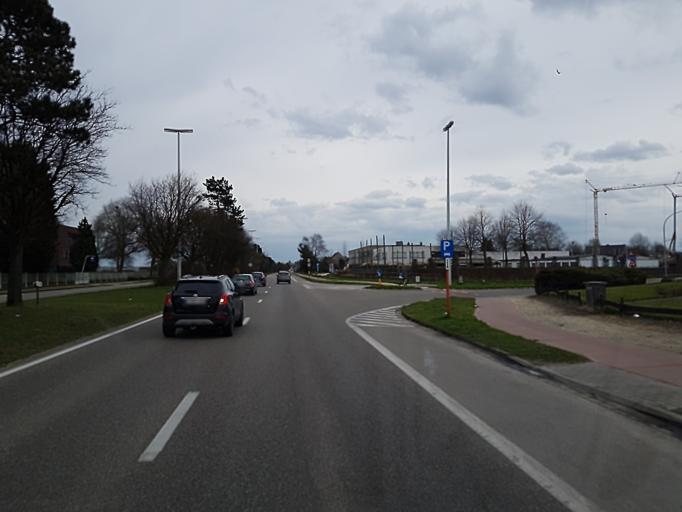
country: BE
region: Flanders
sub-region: Provincie Antwerpen
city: Turnhout
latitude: 51.3320
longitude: 4.9618
